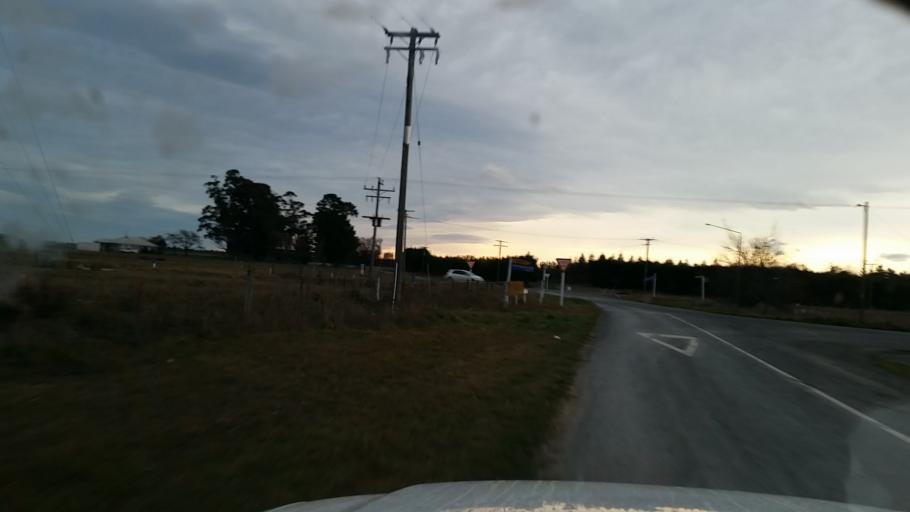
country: NZ
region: Canterbury
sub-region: Ashburton District
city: Tinwald
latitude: -43.8364
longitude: 171.6150
